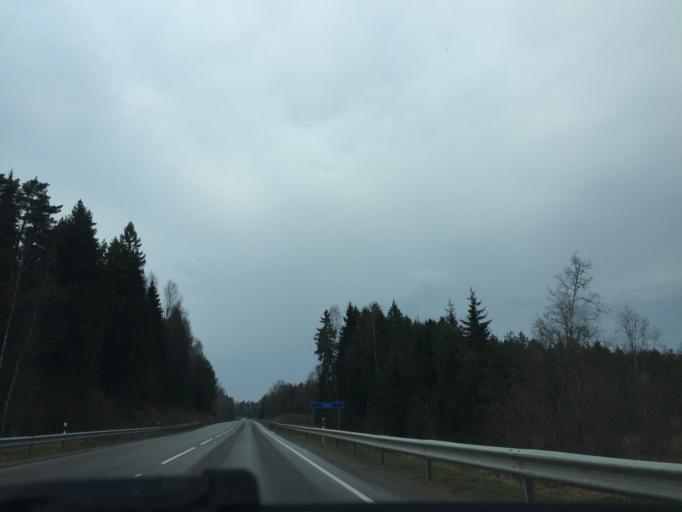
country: EE
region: Tartu
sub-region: UElenurme vald
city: Ulenurme
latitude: 58.1158
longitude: 26.7347
